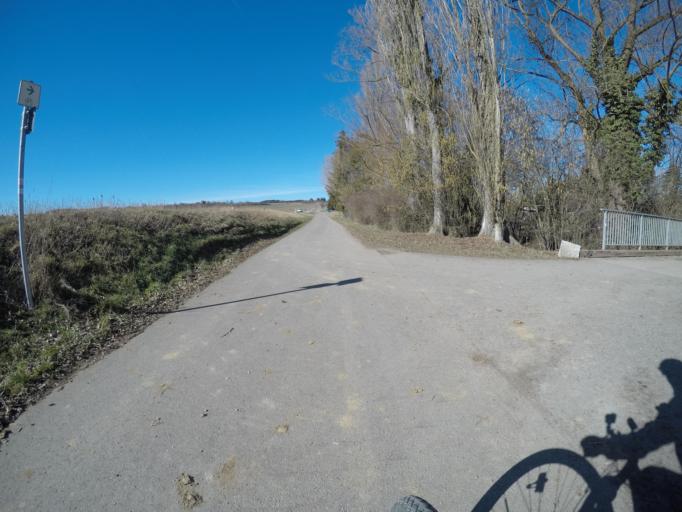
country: DE
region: Baden-Wuerttemberg
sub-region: Regierungsbezirk Stuttgart
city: Herrenberg
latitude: 48.5716
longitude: 8.8719
